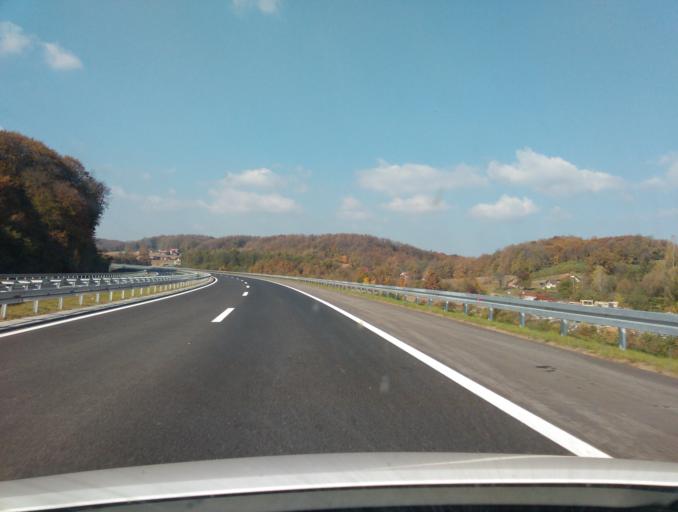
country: BA
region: Republika Srpska
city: Prnjavor
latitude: 44.8928
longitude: 17.6062
